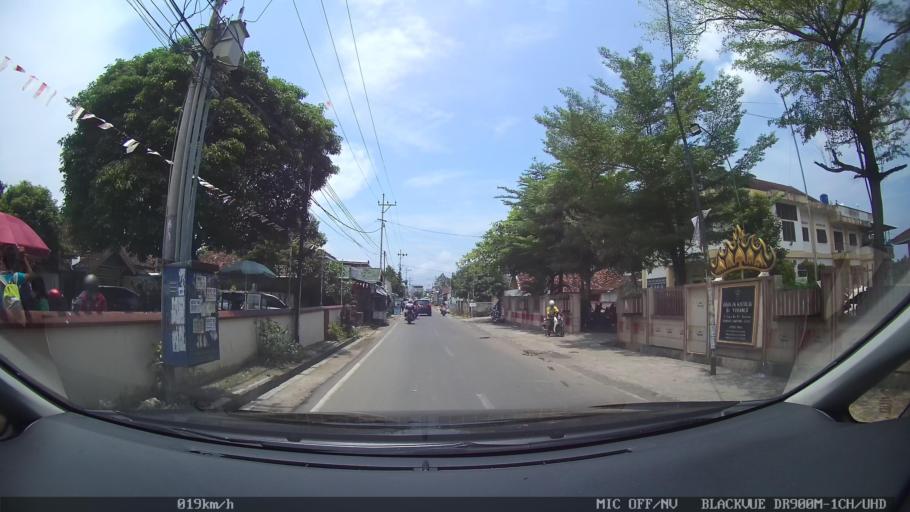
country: ID
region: Lampung
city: Kedaton
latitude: -5.3883
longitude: 105.2585
